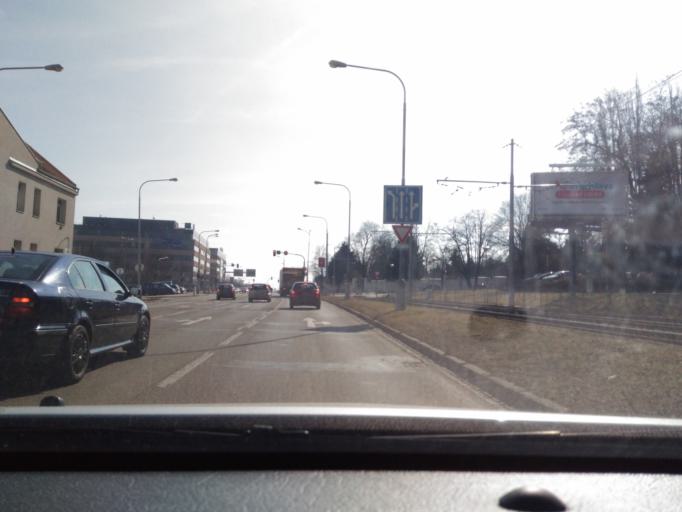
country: CZ
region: South Moravian
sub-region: Mesto Brno
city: Brno
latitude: 49.1736
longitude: 16.5966
